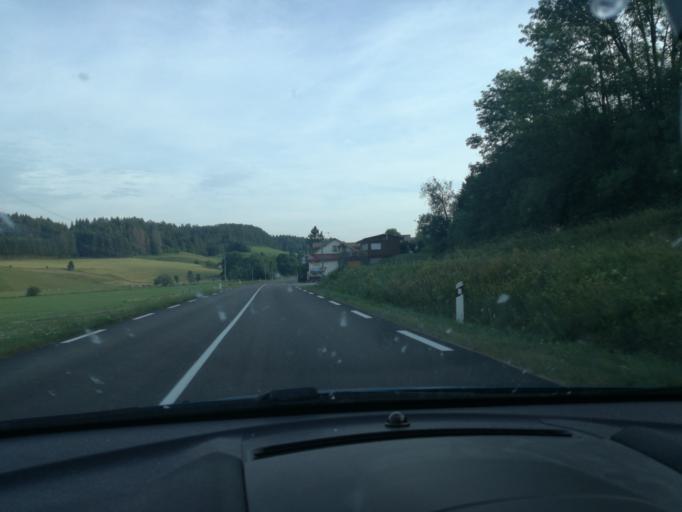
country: FR
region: Franche-Comte
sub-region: Departement du Jura
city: Morbier
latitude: 46.6036
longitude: 5.9620
